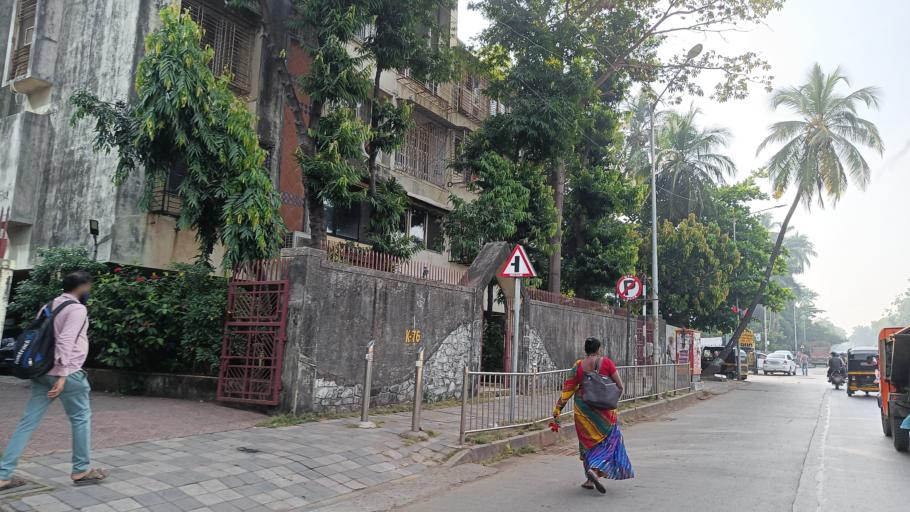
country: IN
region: Maharashtra
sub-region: Mumbai Suburban
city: Mumbai
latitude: 19.0989
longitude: 72.8396
